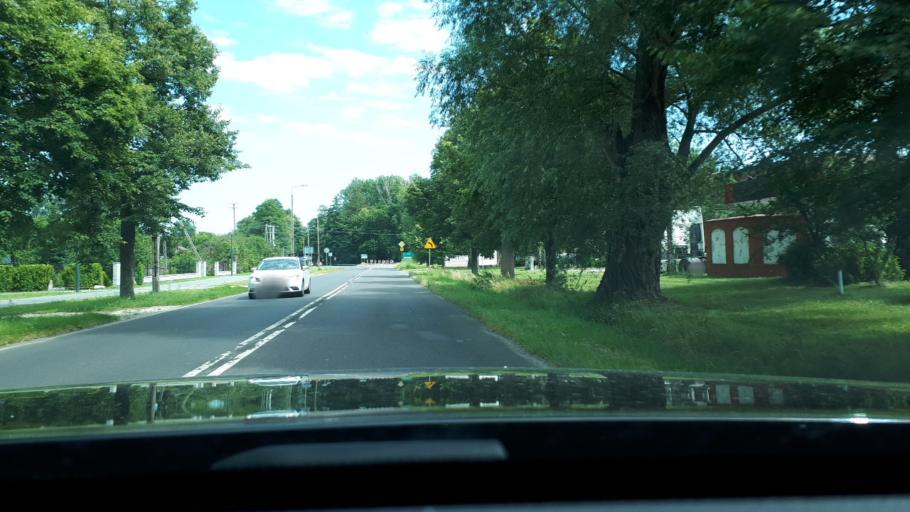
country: PL
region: Lodz Voivodeship
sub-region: powiat Lowicki
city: Nieborow
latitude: 52.0683
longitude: 20.0619
